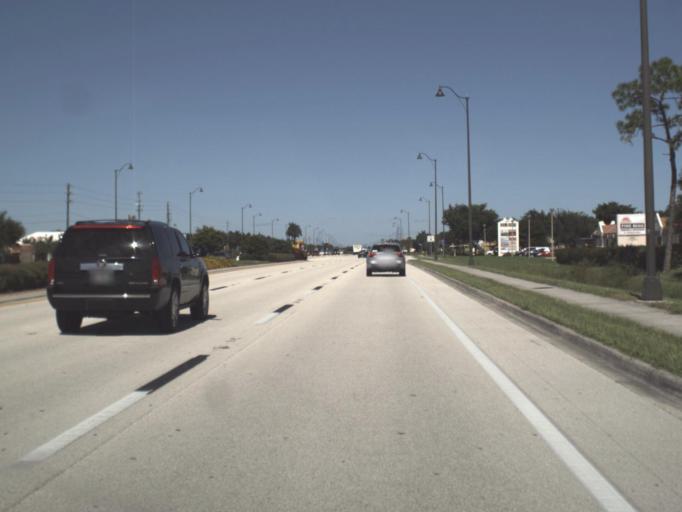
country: US
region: Florida
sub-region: Lee County
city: Bonita Springs
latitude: 26.3219
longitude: -81.8052
